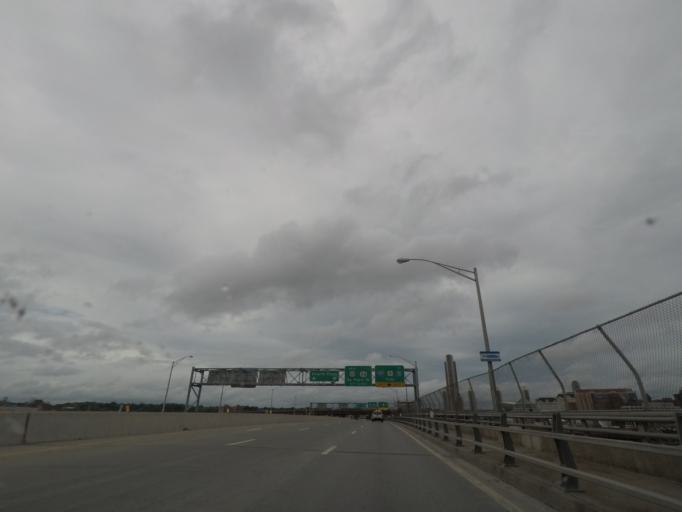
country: US
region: New York
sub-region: Rensselaer County
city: Rensselaer
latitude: 42.6430
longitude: -73.7466
